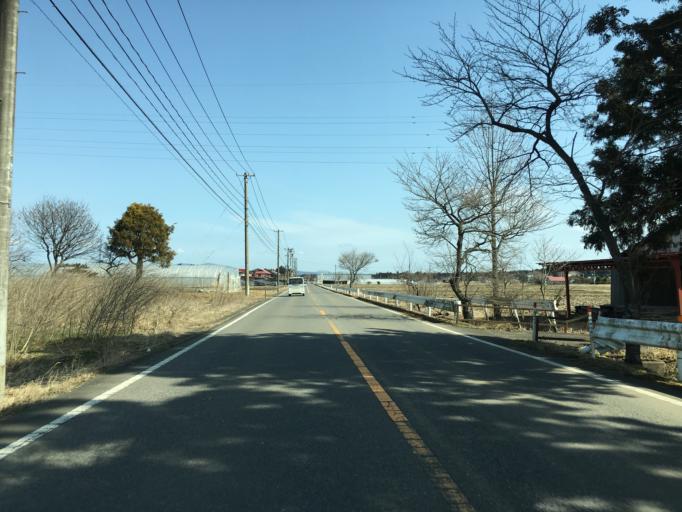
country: JP
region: Fukushima
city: Ishikawa
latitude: 37.1394
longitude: 140.3374
